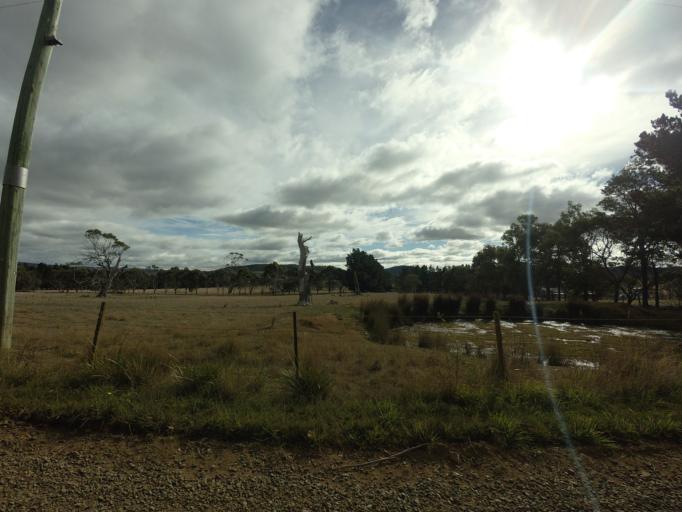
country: AU
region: Tasmania
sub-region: Brighton
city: Bridgewater
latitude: -42.4123
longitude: 147.3988
